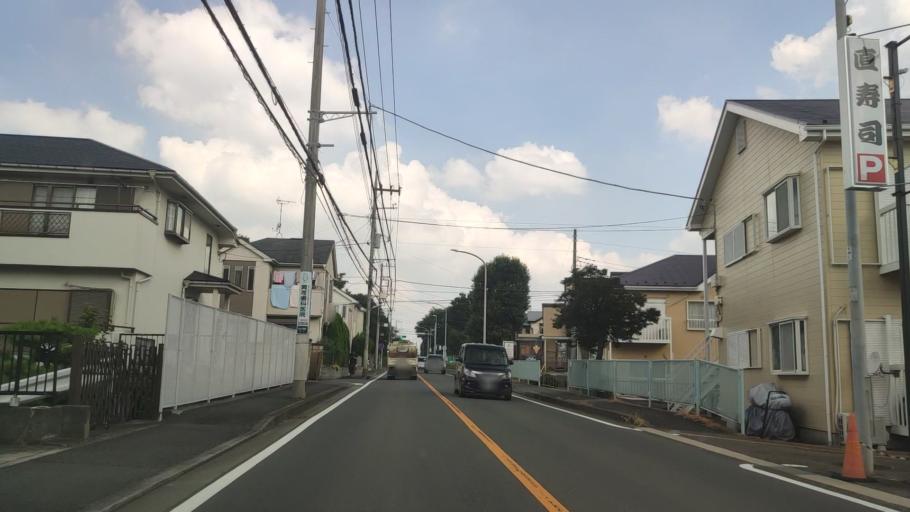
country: JP
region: Kanagawa
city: Minami-rinkan
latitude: 35.4534
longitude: 139.5023
